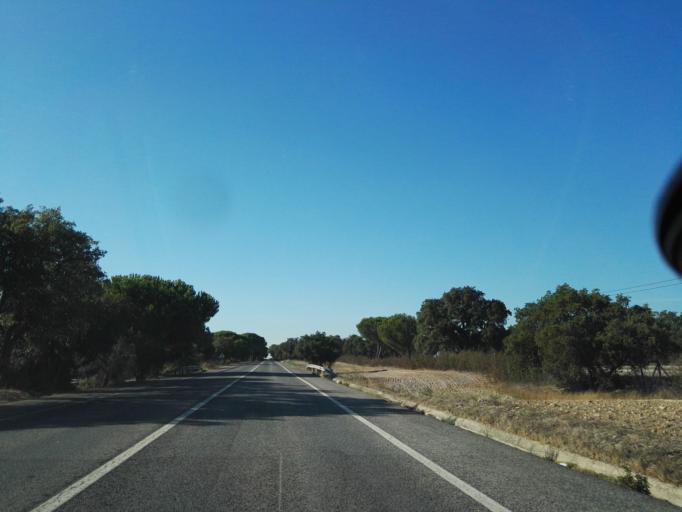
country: PT
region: Santarem
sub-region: Benavente
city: Poceirao
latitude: 38.8581
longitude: -8.7782
